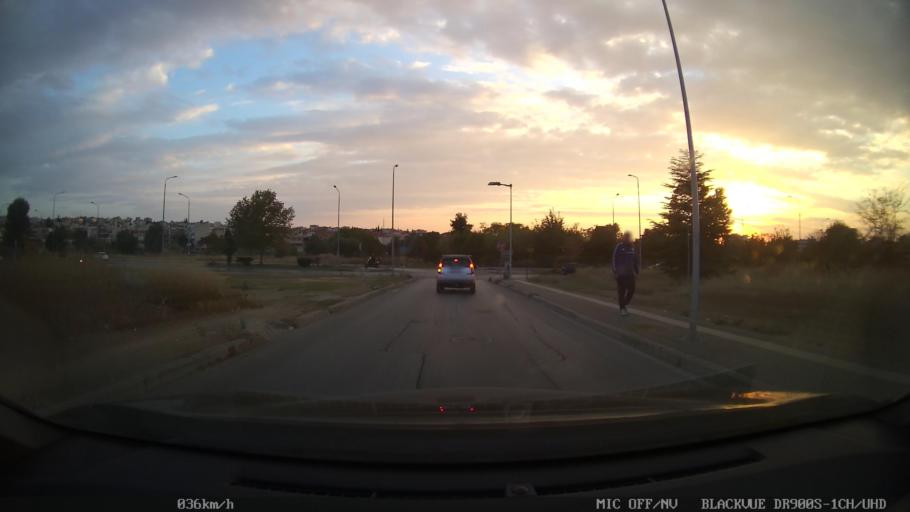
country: GR
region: Central Macedonia
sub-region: Nomos Thessalonikis
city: Pylaia
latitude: 40.6058
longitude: 22.9876
